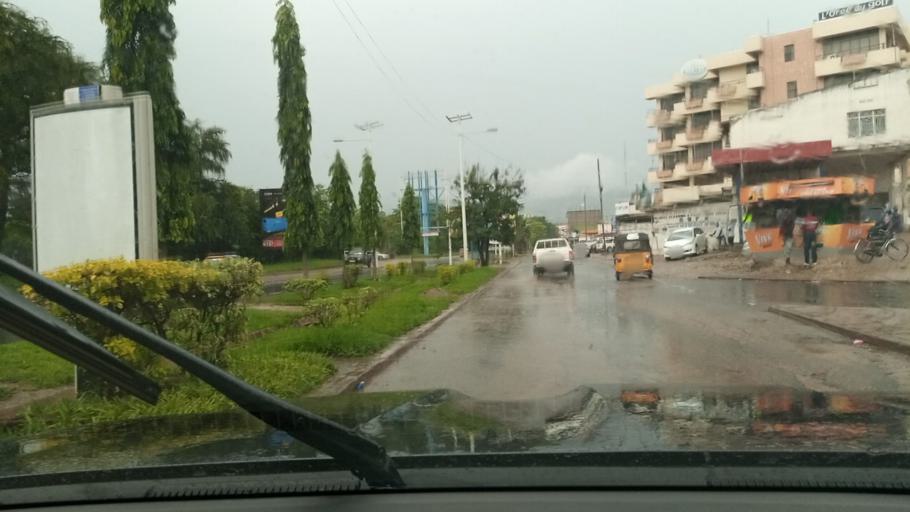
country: BI
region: Bujumbura Mairie
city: Bujumbura
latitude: -3.3789
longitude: 29.3536
